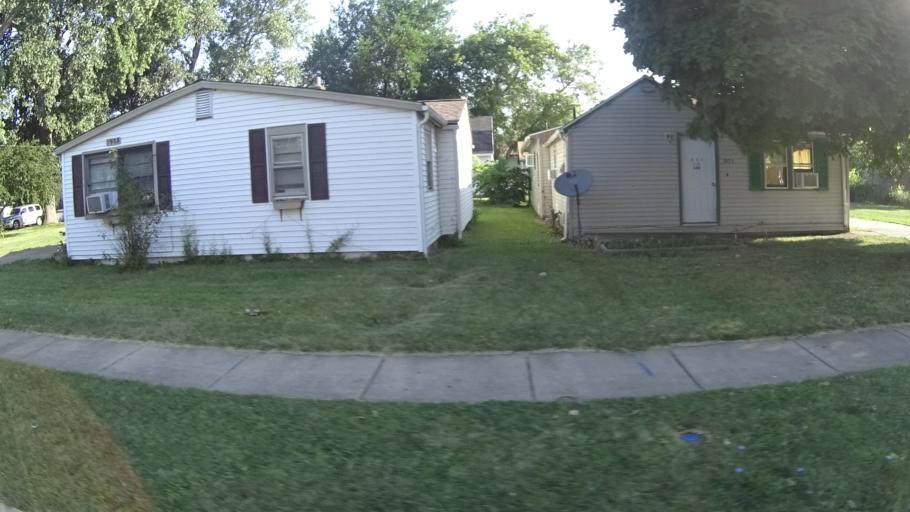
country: US
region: Ohio
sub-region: Erie County
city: Sandusky
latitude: 41.4472
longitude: -82.6795
